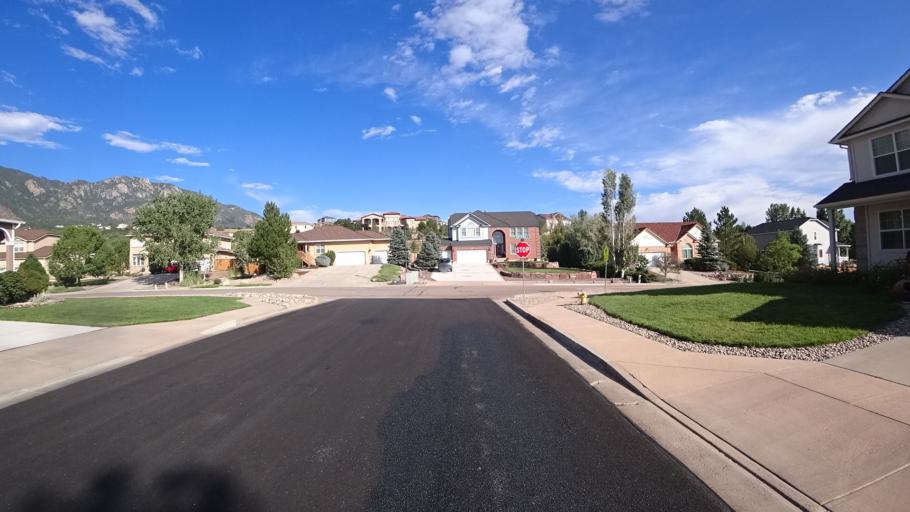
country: US
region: Colorado
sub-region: El Paso County
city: Fort Carson
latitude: 38.7552
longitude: -104.8160
